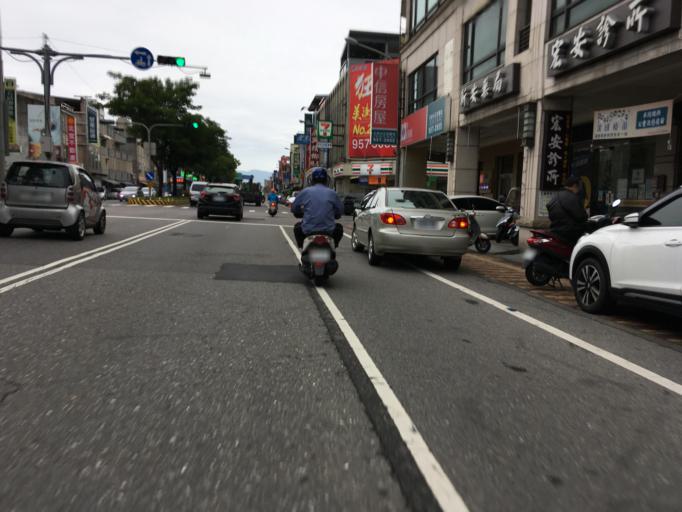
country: TW
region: Taiwan
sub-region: Yilan
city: Yilan
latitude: 24.6907
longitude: 121.7703
